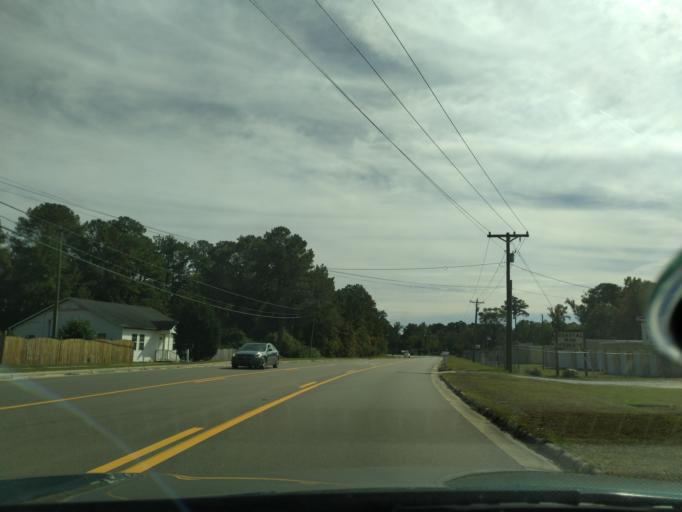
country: US
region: North Carolina
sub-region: Beaufort County
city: River Road
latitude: 35.5184
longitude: -77.0048
